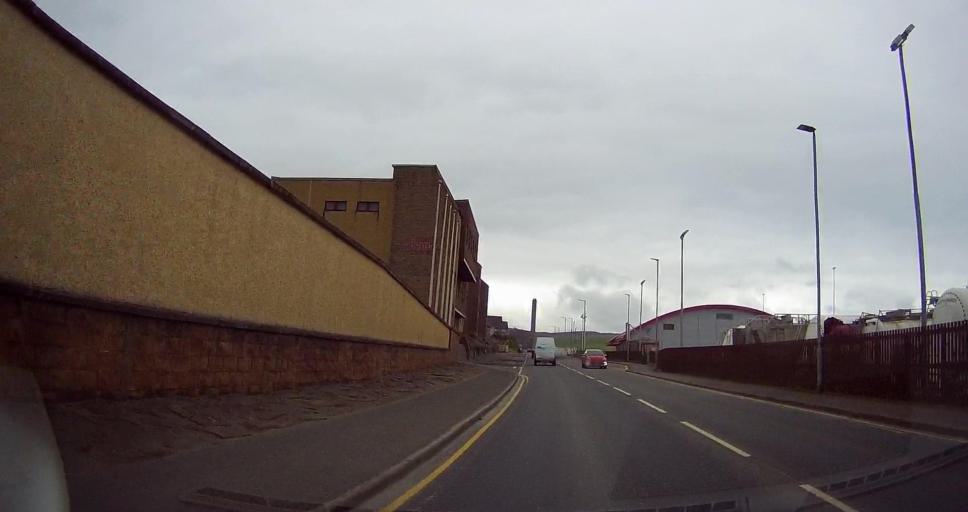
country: GB
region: Scotland
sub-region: Shetland Islands
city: Lerwick
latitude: 60.1612
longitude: -1.1580
